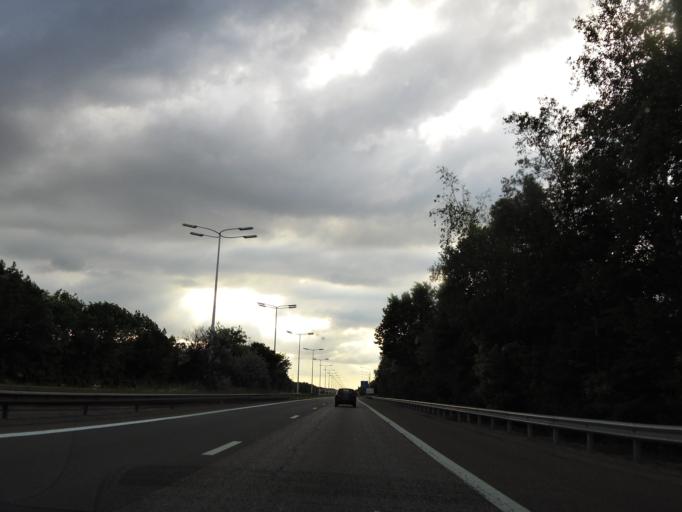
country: BE
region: Flanders
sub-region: Provincie Limburg
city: Genk
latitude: 50.9891
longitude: 5.5113
